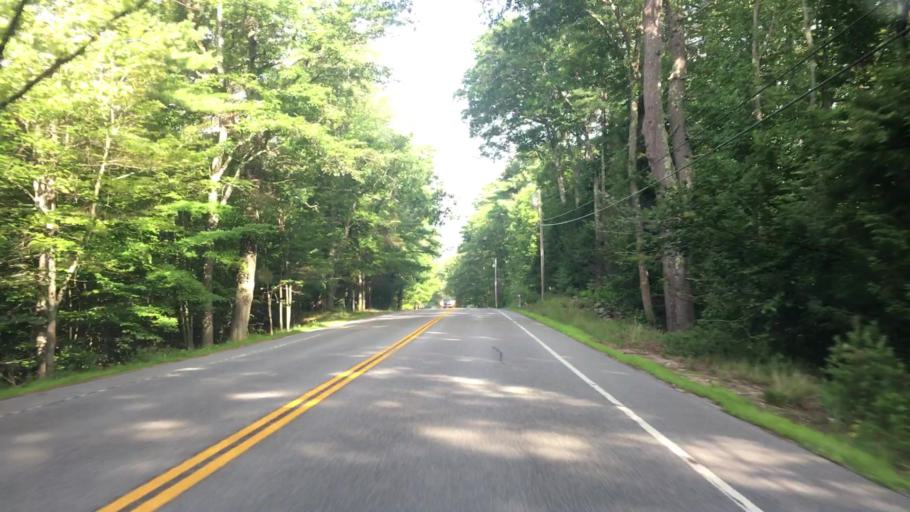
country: US
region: Maine
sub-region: York County
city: Limington
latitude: 43.7778
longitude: -70.7451
